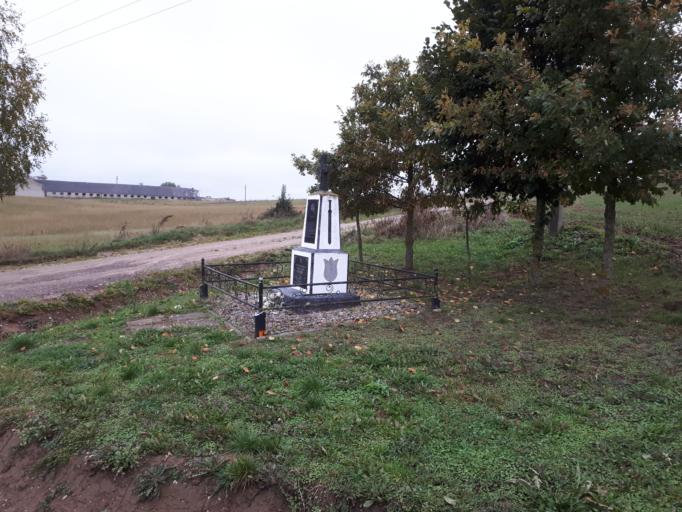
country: PL
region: Podlasie
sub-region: Powiat sejnenski
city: Punsk
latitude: 54.3731
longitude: 23.0539
